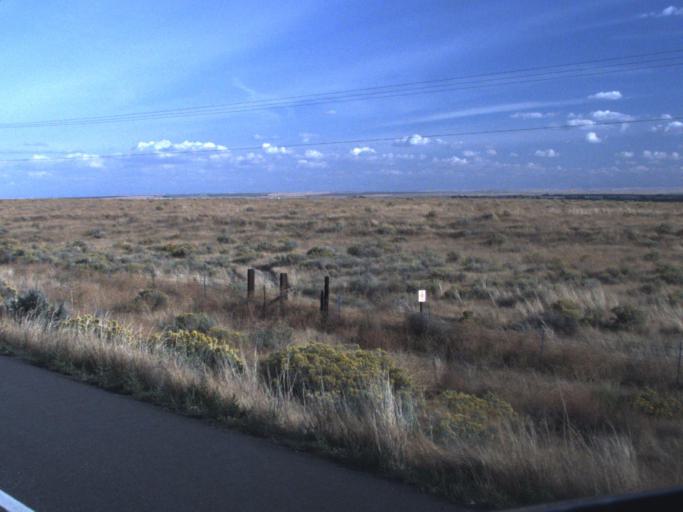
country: US
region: Oregon
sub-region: Morrow County
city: Irrigon
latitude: 45.9403
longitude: -119.5736
